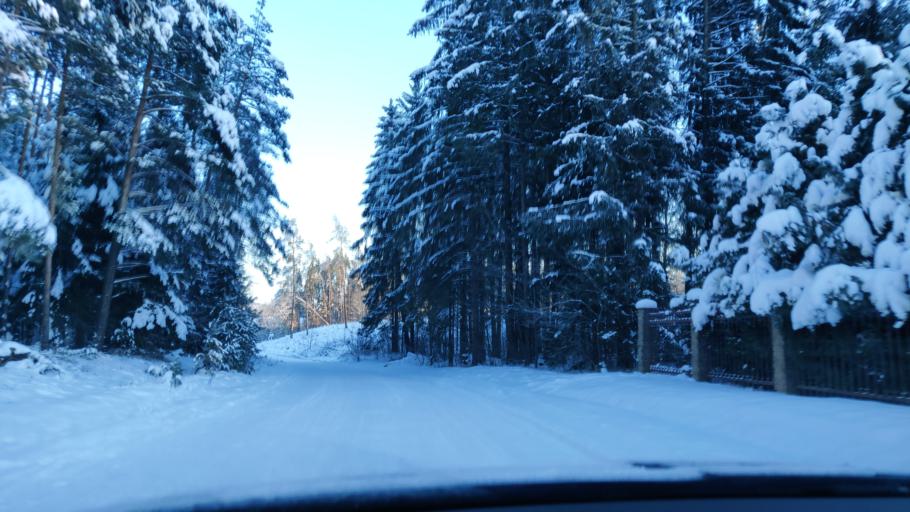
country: LT
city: Trakai
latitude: 54.6140
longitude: 24.9293
